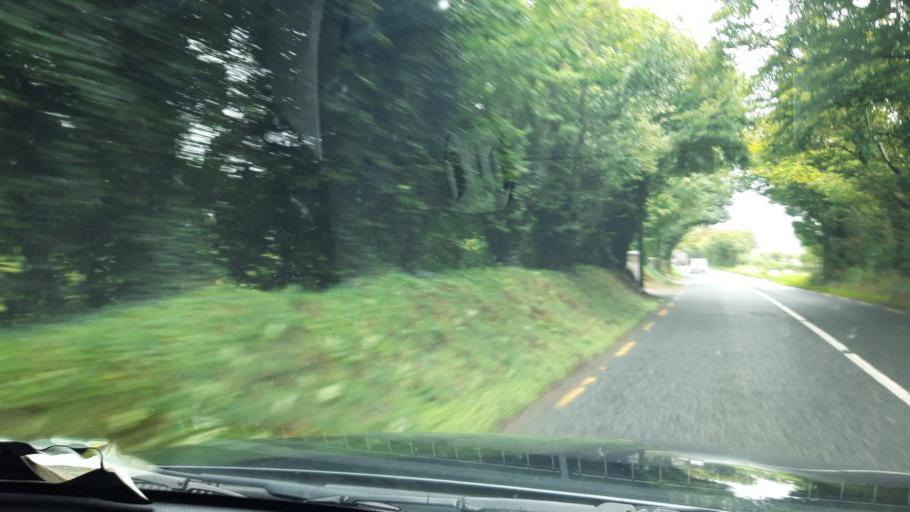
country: IE
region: Leinster
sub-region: Loch Garman
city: New Ross
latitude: 52.4333
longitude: -6.7602
